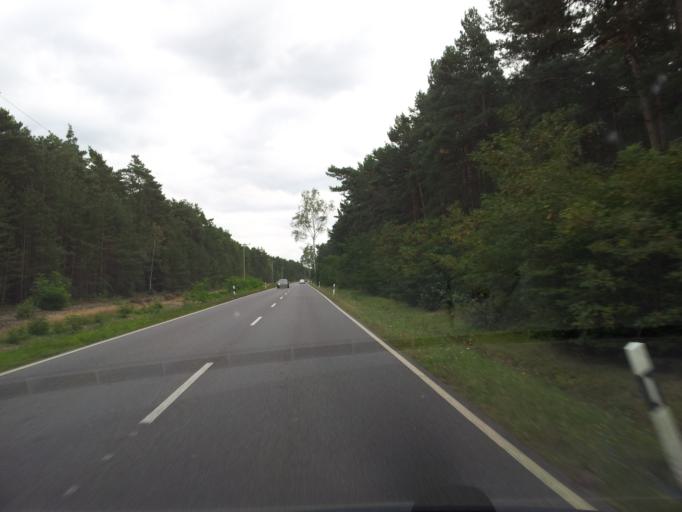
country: DE
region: Brandenburg
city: Guteborn
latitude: 51.4119
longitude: 13.9517
